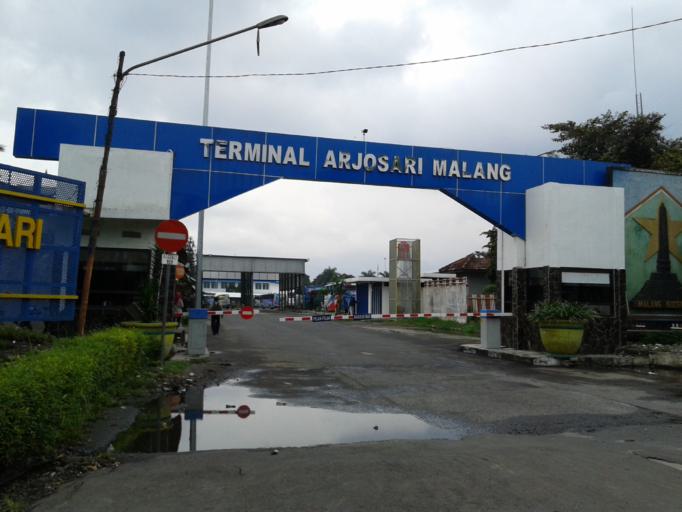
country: ID
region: East Java
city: Singosari
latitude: -7.9341
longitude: 112.6546
